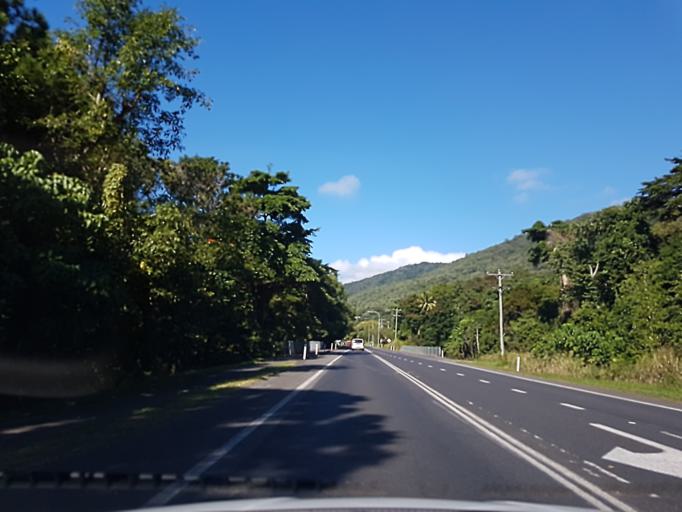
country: AU
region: Queensland
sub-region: Cairns
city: Palm Cove
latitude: -16.7488
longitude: 145.6627
